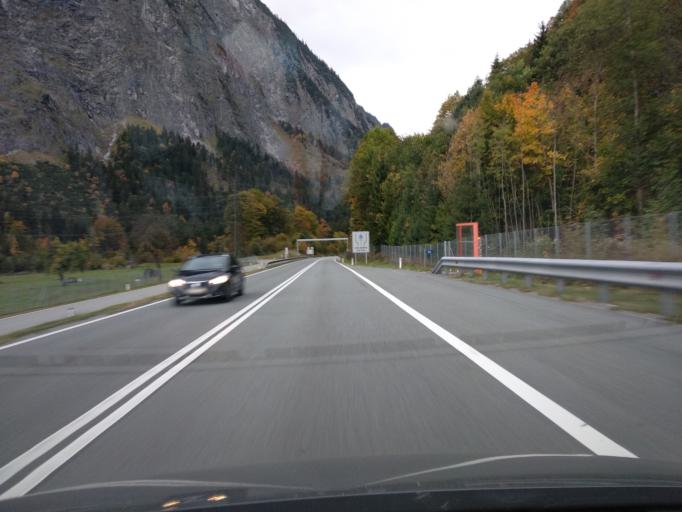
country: AT
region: Vorarlberg
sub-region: Politischer Bezirk Bludenz
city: Dalaas
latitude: 47.1306
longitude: 9.9561
